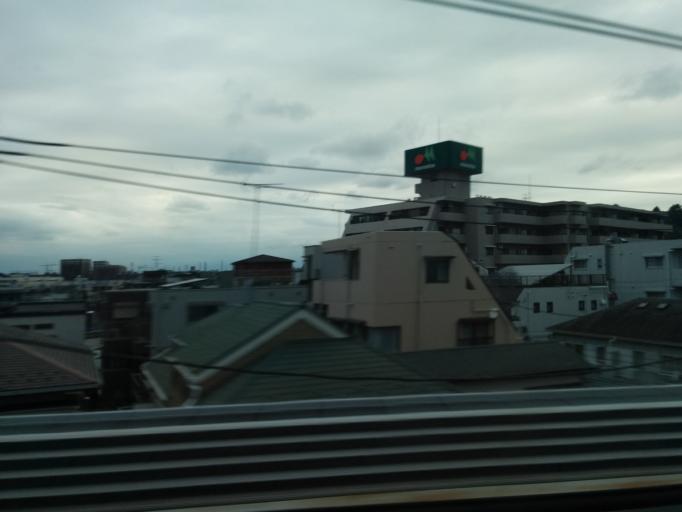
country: JP
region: Kanagawa
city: Yokohama
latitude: 35.5195
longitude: 139.6308
